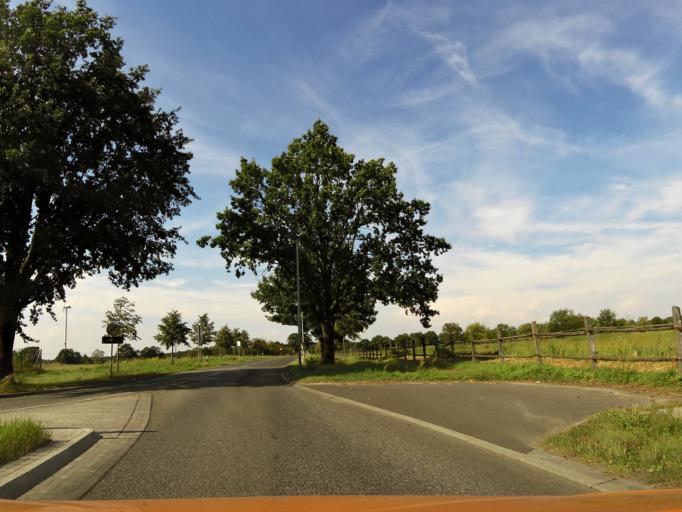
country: DE
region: Brandenburg
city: Grossbeeren
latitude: 52.3516
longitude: 13.2735
